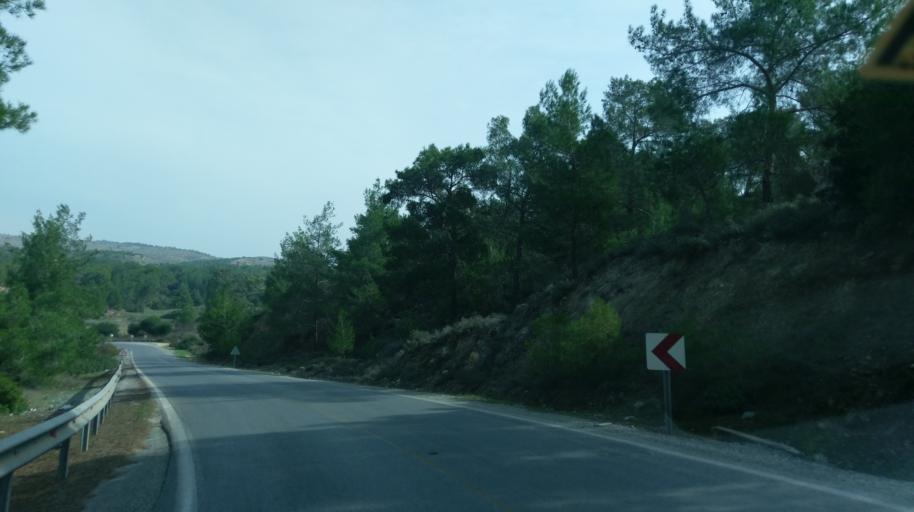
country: CY
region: Lefkosia
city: Morfou
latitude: 35.2547
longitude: 33.0389
